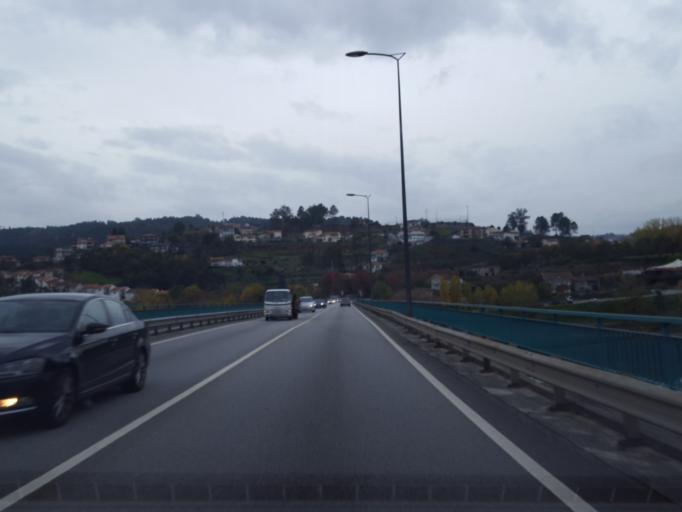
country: PT
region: Porto
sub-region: Marco de Canaveses
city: Marco de Canavezes
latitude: 41.1946
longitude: -8.1578
